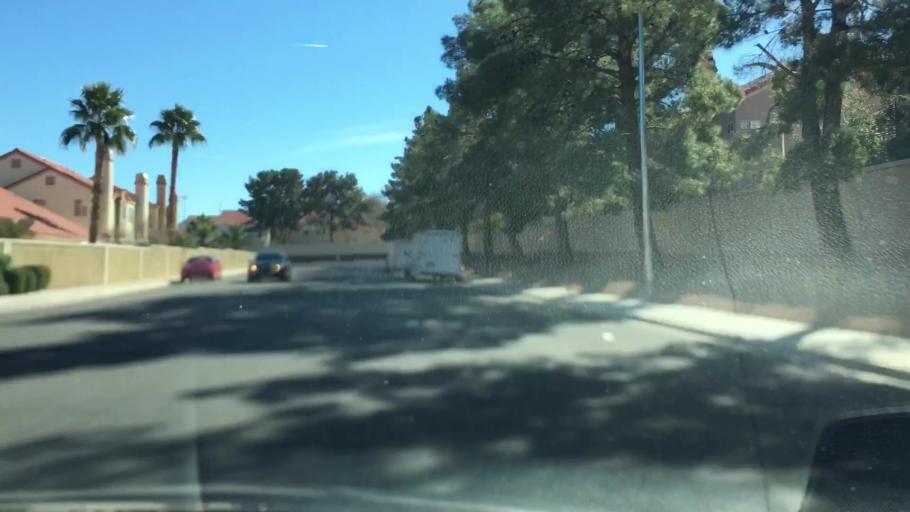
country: US
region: Nevada
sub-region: Clark County
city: Whitney
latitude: 36.0623
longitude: -115.0610
